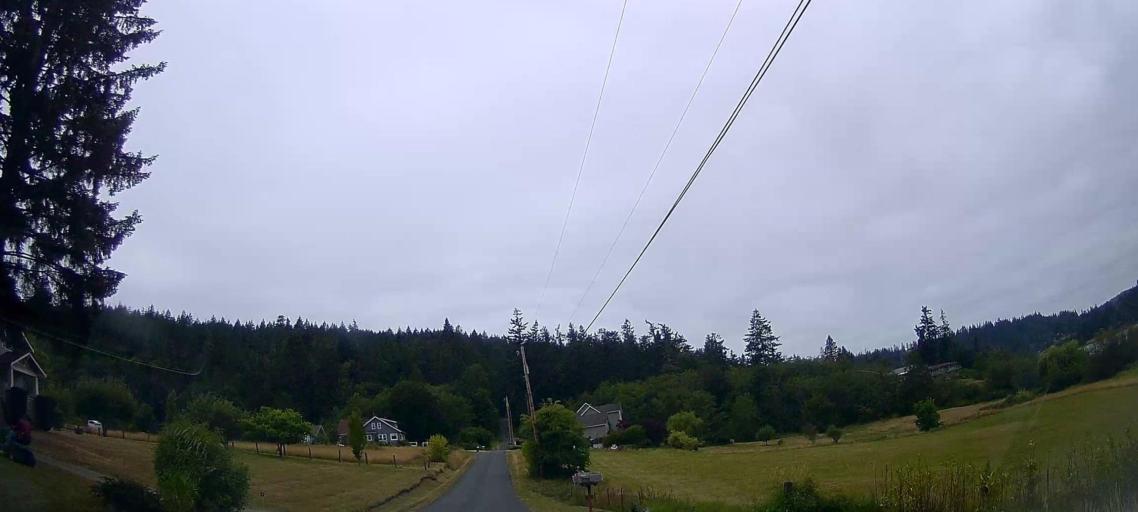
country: US
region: Washington
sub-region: Skagit County
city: Anacortes
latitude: 48.4336
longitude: -122.6197
